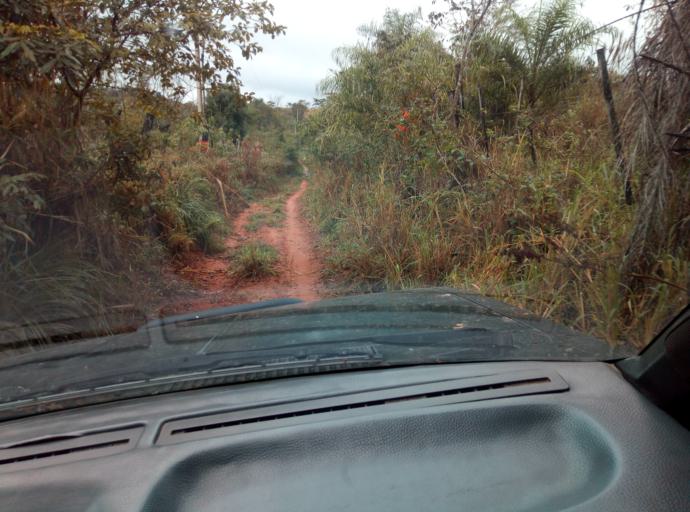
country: PY
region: Caaguazu
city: Carayao
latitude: -25.1958
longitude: -56.3544
